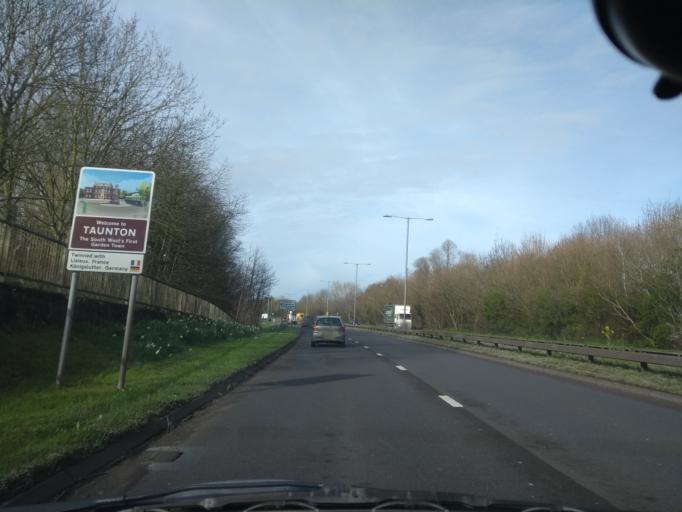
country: GB
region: England
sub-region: Somerset
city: Taunton
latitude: 51.0249
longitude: -3.0770
